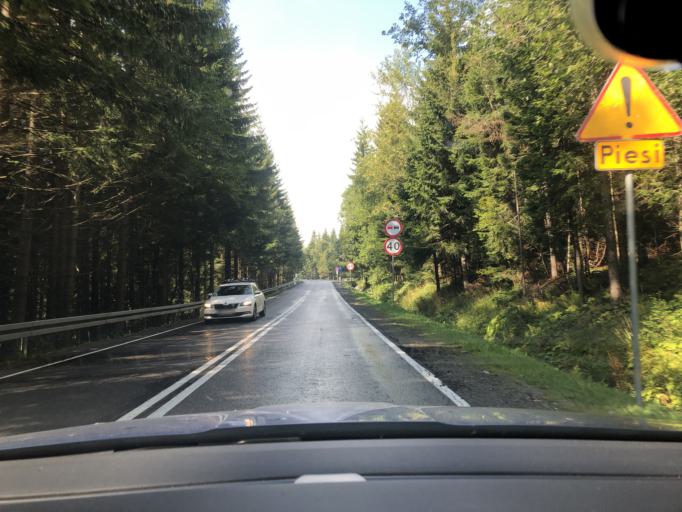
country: PL
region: Lesser Poland Voivodeship
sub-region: Powiat nowotarski
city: Zubrzyca Gorna
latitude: 49.5871
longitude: 19.5868
